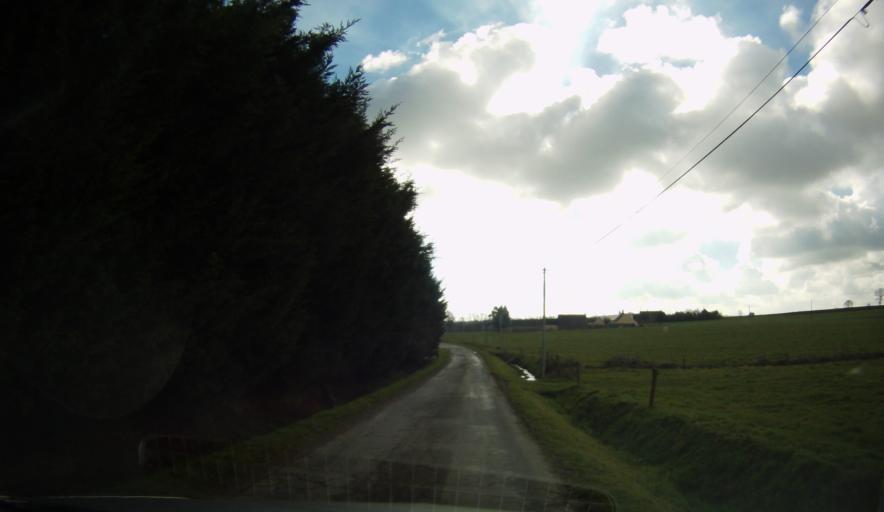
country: FR
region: Brittany
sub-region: Departement d'Ille-et-Vilaine
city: Chanteloup
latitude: 47.9499
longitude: -1.5996
